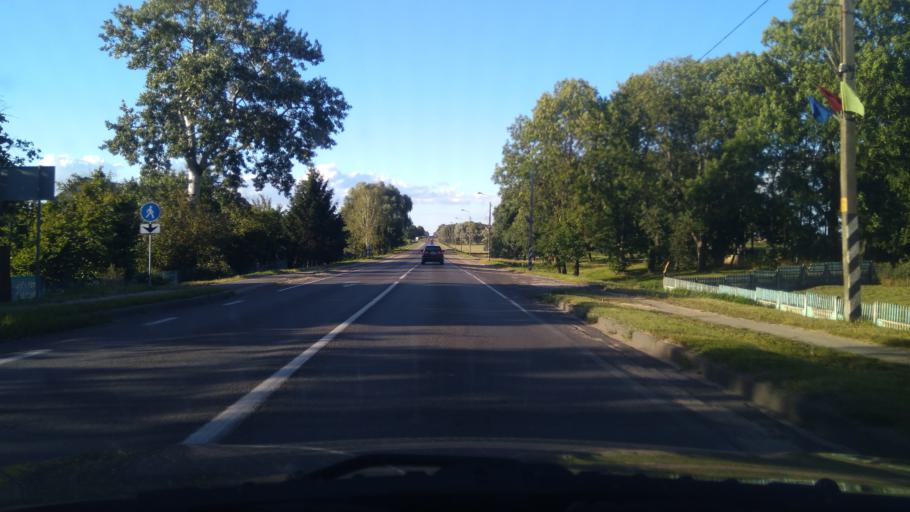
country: BY
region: Brest
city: Pruzhany
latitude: 52.5553
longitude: 24.4763
